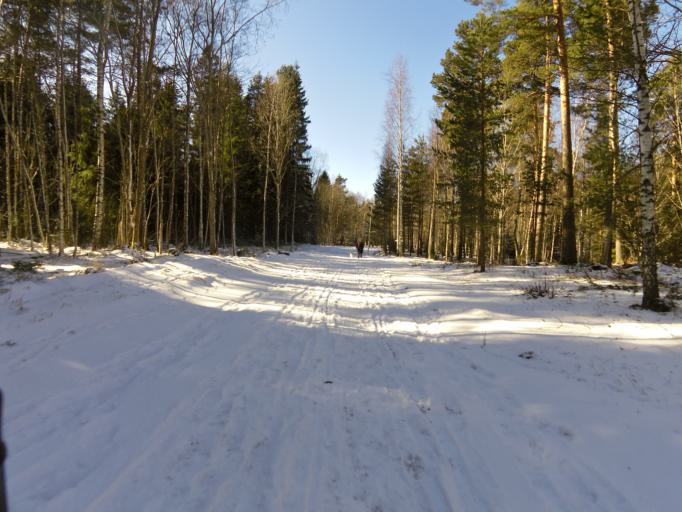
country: SE
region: Gaevleborg
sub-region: Gavle Kommun
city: Gavle
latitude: 60.6635
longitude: 17.2353
